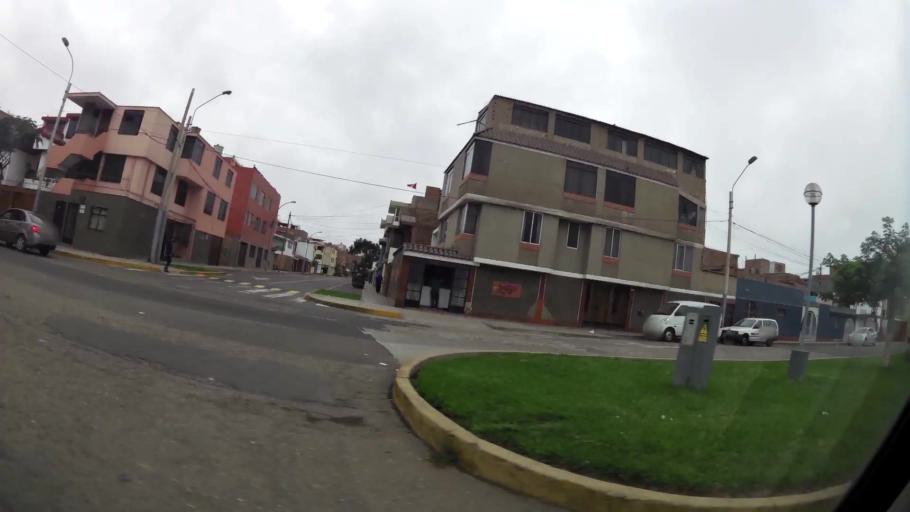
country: PE
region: Callao
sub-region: Callao
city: Callao
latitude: -12.0703
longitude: -77.1045
